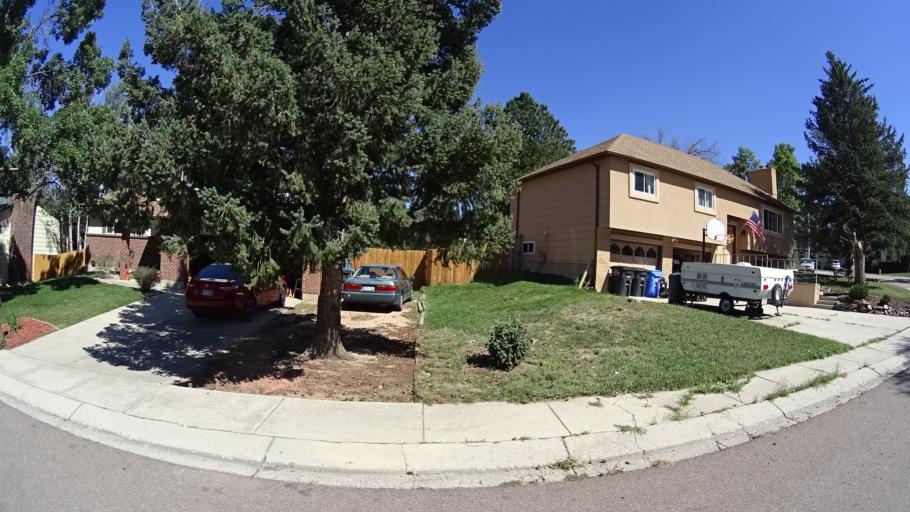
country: US
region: Colorado
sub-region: El Paso County
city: Cimarron Hills
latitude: 38.8760
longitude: -104.7385
